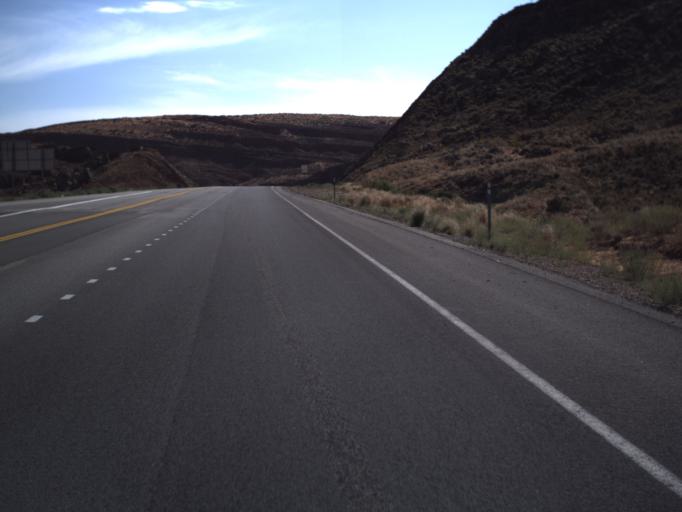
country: US
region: Utah
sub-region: Washington County
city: Washington
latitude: 37.1136
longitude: -113.4459
